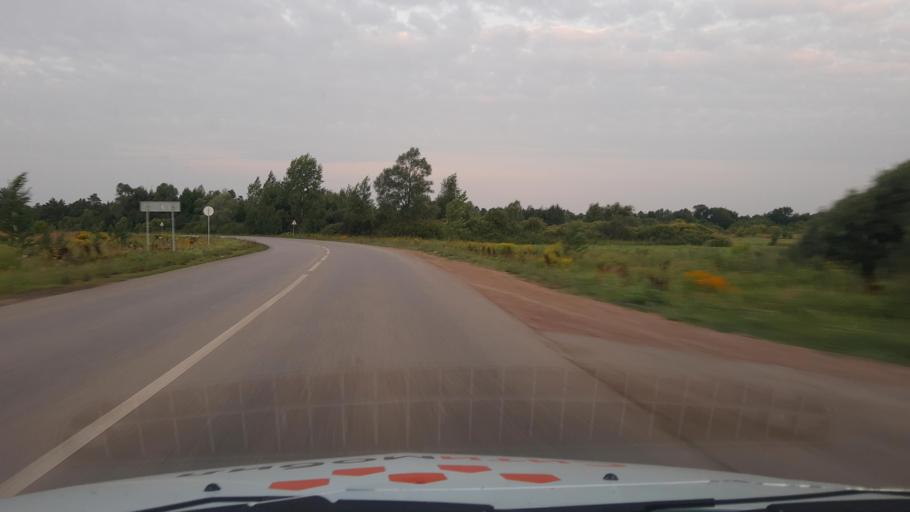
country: RU
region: Bashkortostan
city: Kabakovo
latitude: 54.7341
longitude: 56.1963
